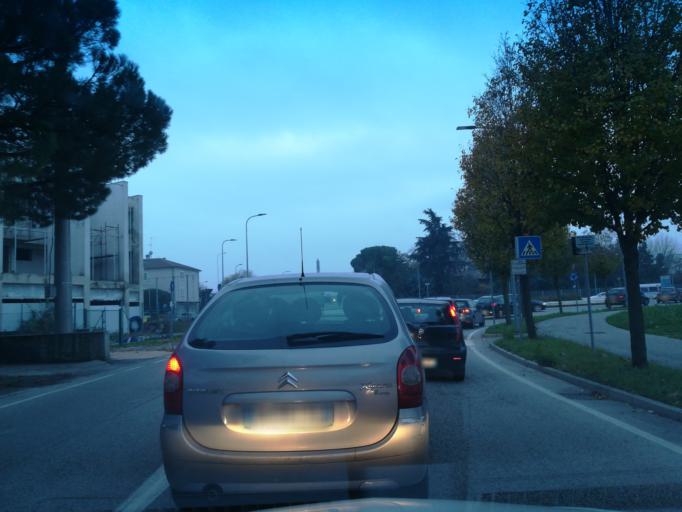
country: IT
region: Emilia-Romagna
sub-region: Provincia di Ravenna
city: Faenza
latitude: 44.2963
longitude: 11.8886
